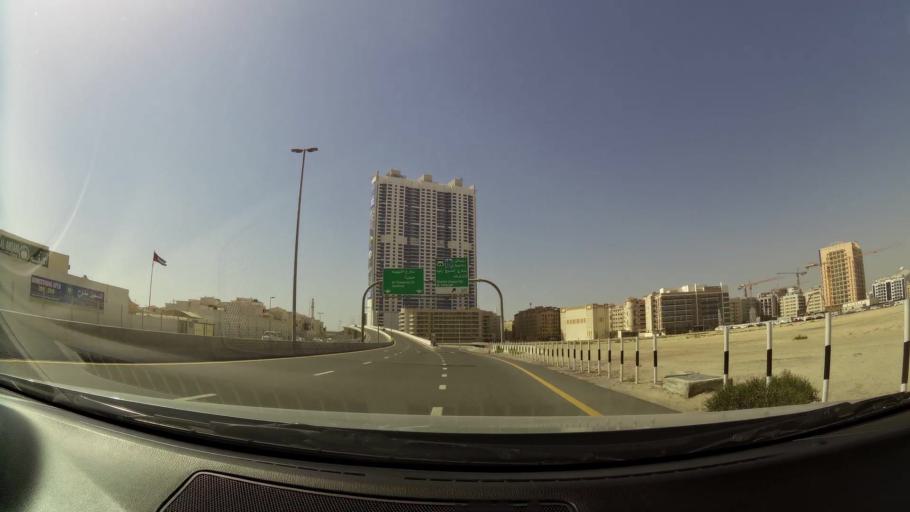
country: AE
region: Dubai
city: Dubai
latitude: 25.1084
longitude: 55.1901
